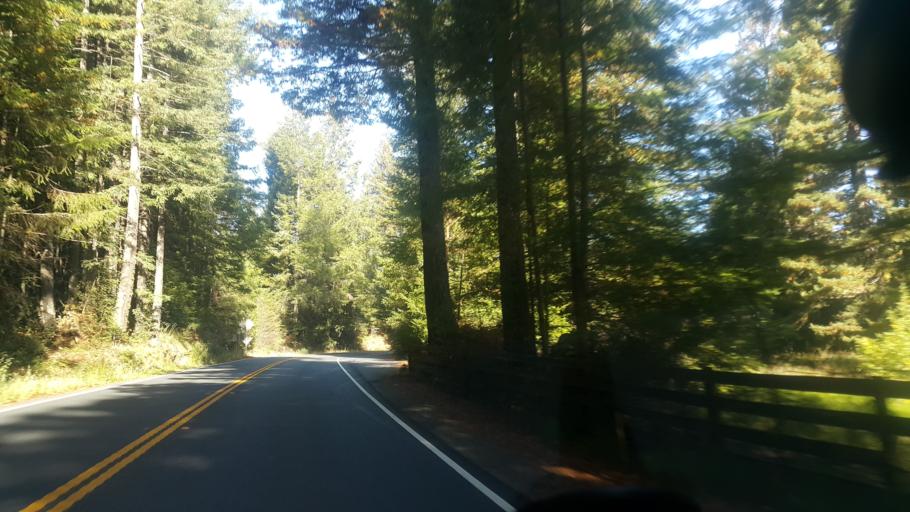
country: US
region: California
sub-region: Mendocino County
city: Fort Bragg
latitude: 39.3507
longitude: -123.6063
